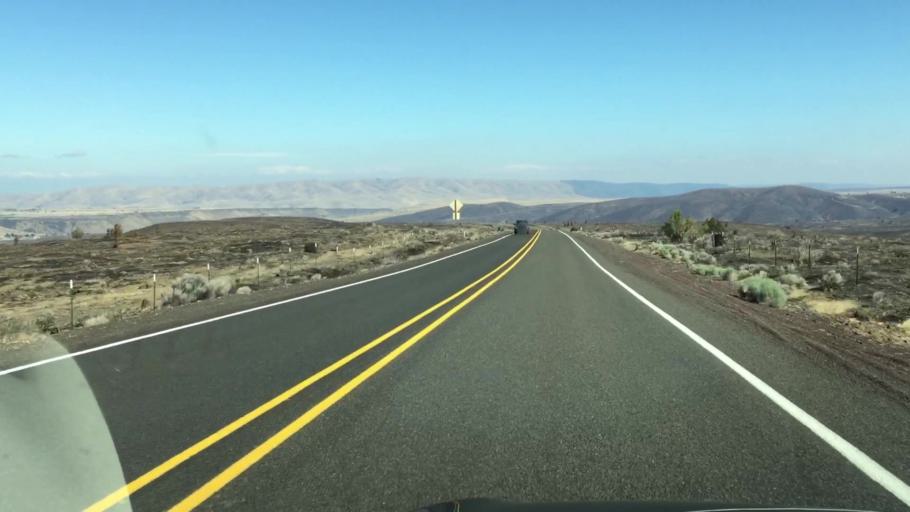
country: US
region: Oregon
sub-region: Jefferson County
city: Warm Springs
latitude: 45.1207
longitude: -121.0467
